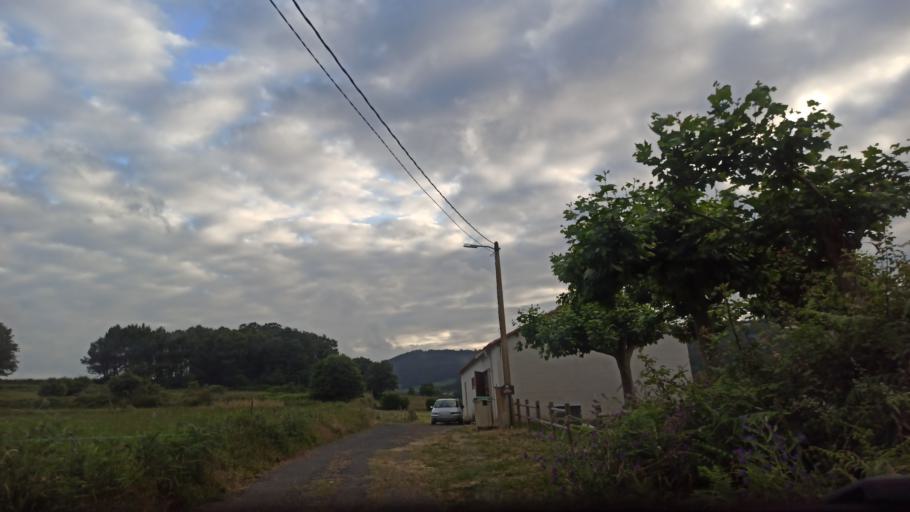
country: ES
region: Galicia
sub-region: Provincia da Coruna
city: Santiso
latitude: 42.8359
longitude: -8.1231
